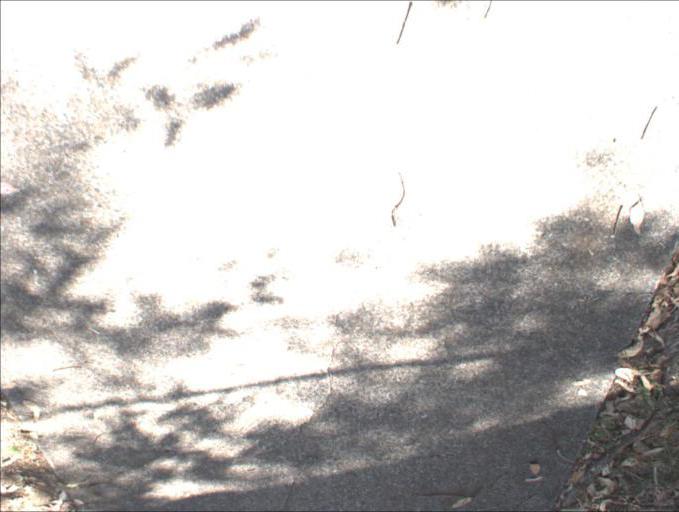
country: AU
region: Queensland
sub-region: Logan
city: Slacks Creek
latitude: -27.6414
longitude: 153.1567
